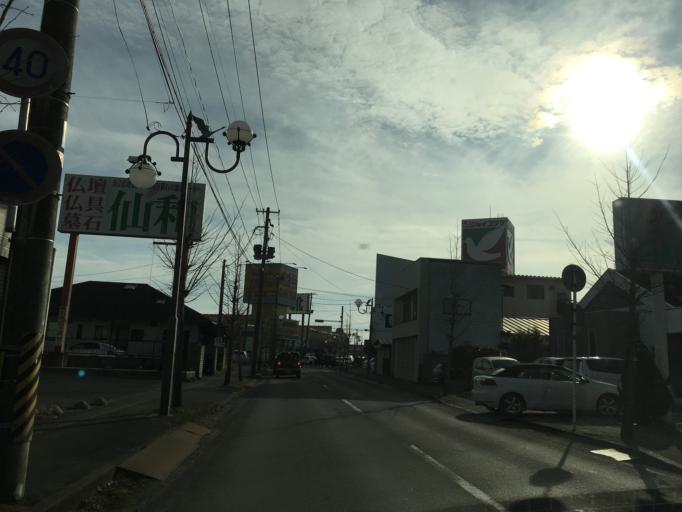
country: JP
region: Miyagi
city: Wakuya
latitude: 38.6924
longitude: 141.1910
